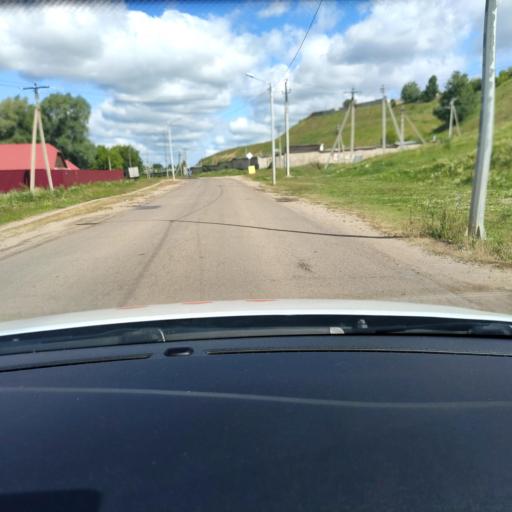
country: RU
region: Tatarstan
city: Vysokaya Gora
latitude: 55.8565
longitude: 49.2452
